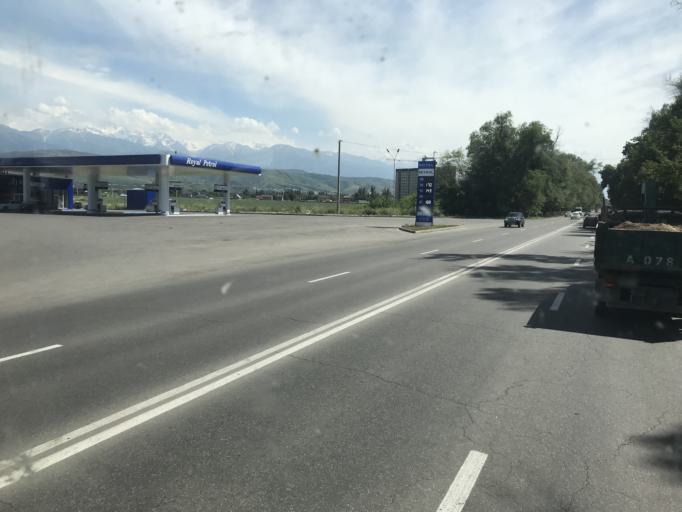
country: KZ
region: Almaty Oblysy
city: Energeticheskiy
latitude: 43.3286
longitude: 77.0331
